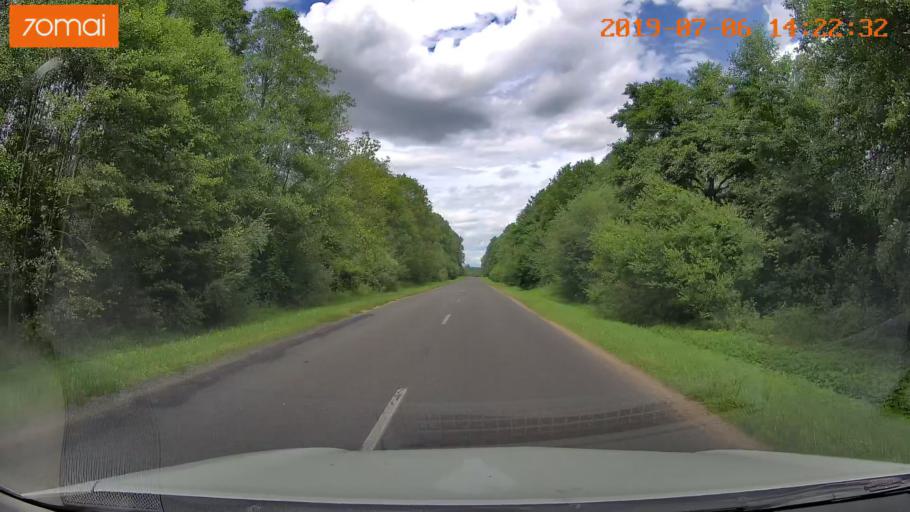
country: BY
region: Minsk
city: Ivyanyets
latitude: 53.9095
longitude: 26.7639
